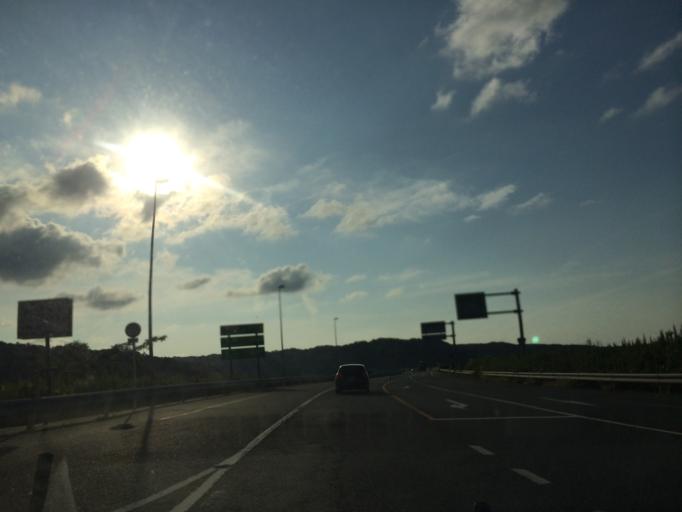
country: JP
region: Tottori
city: Kurayoshi
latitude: 35.5124
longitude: 134.0034
